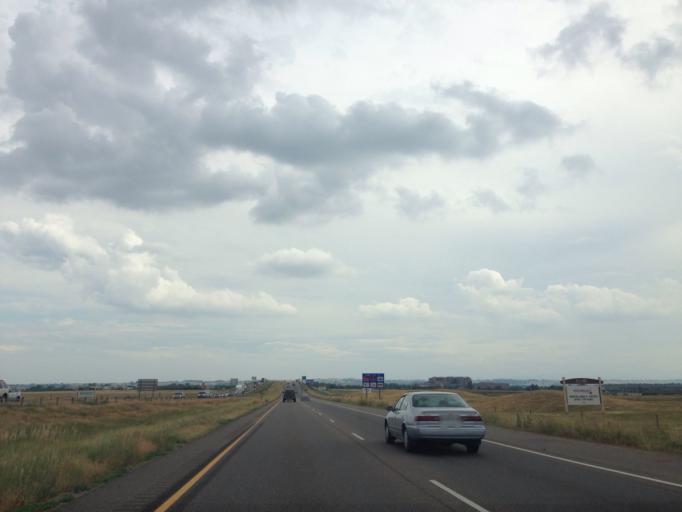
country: US
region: Colorado
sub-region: Larimer County
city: Loveland
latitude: 40.4297
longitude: -104.9926
